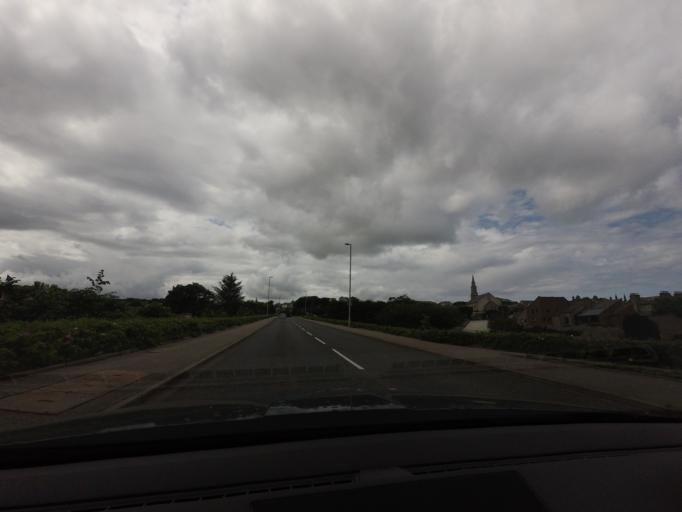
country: GB
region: Scotland
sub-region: Aberdeenshire
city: Banff
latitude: 57.6621
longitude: -2.5192
